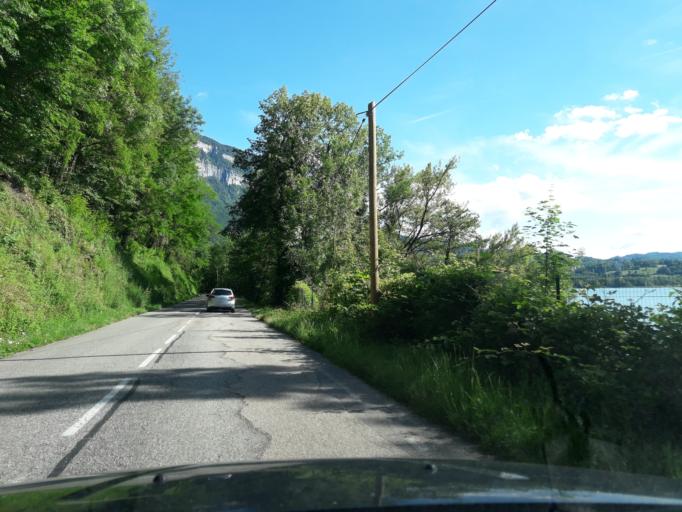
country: FR
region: Rhone-Alpes
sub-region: Departement de la Savoie
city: Vimines
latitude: 45.5531
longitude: 5.8094
